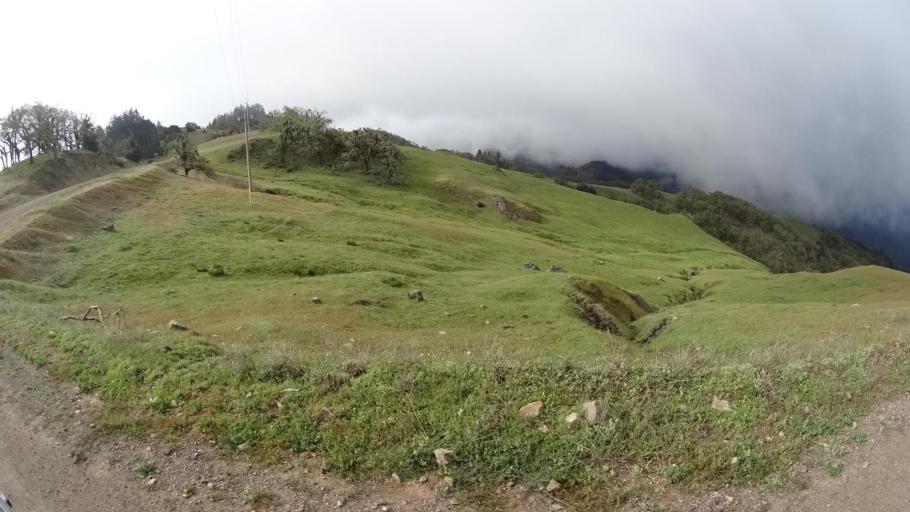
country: US
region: California
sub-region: Humboldt County
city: Redway
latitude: 40.1985
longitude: -123.7078
